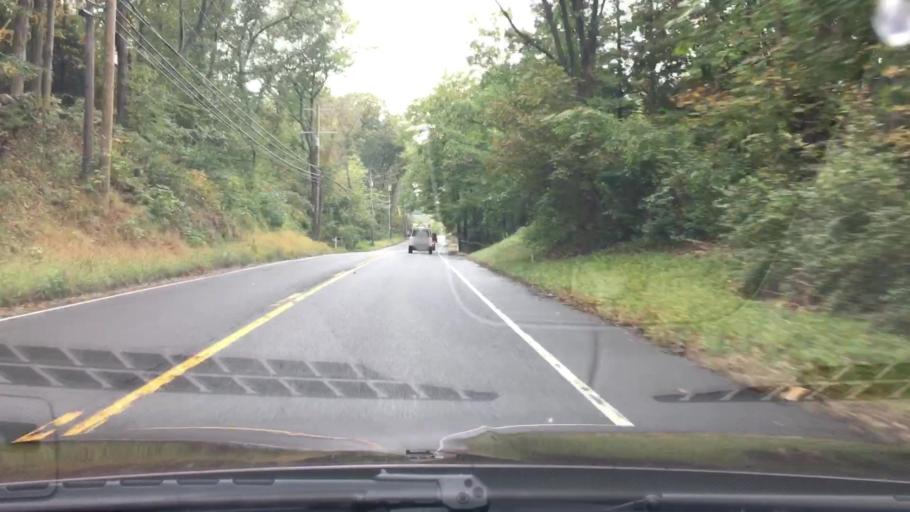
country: US
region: Connecticut
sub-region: Fairfield County
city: Wilton
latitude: 41.1795
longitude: -73.4088
